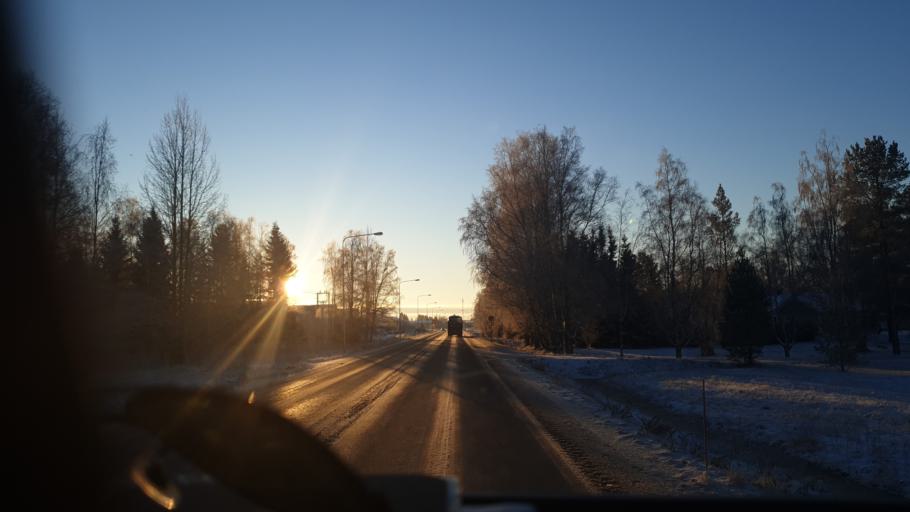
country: FI
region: Northern Ostrobothnia
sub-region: Ylivieska
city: Kalajoki
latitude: 64.2694
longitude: 23.9491
